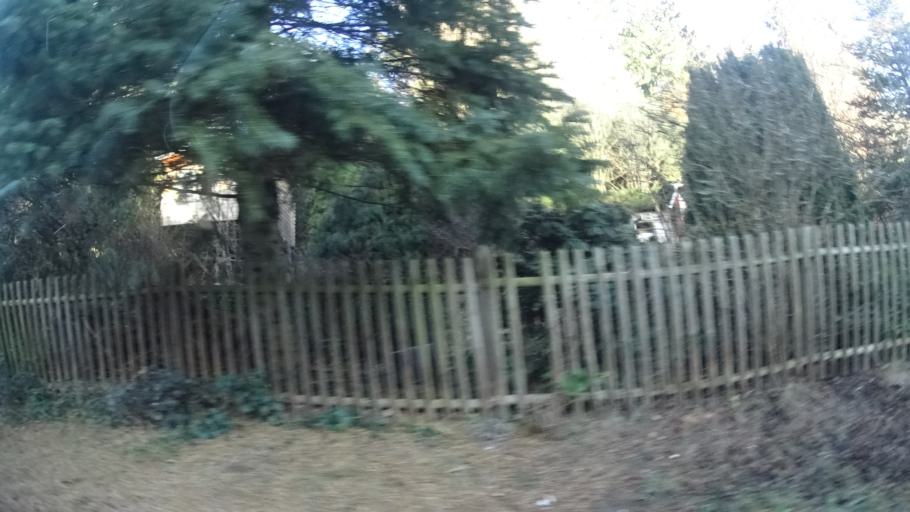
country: DE
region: Thuringia
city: Stadtroda
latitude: 50.8507
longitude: 11.7169
